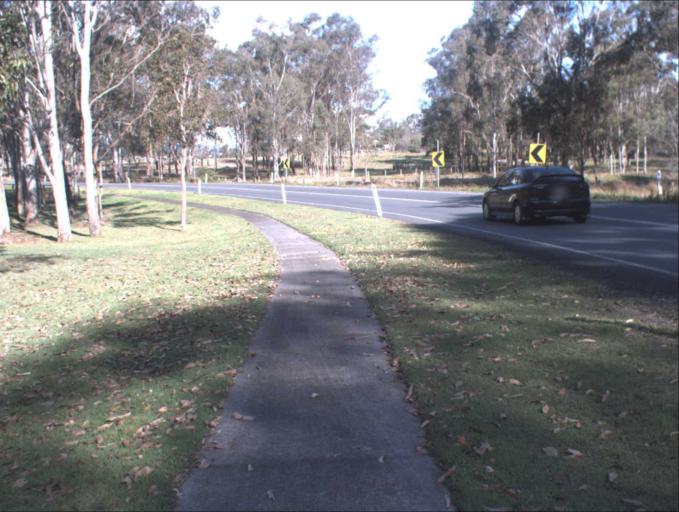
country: AU
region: Queensland
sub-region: Logan
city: Chambers Flat
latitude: -27.7632
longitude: 153.0932
